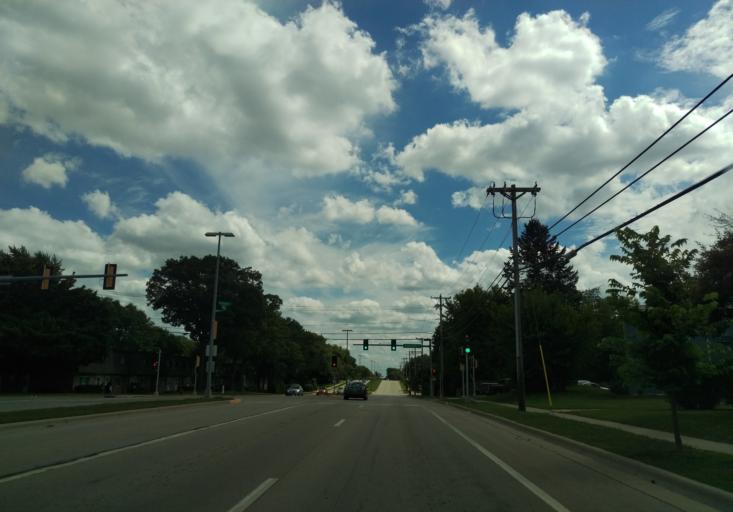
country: US
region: Wisconsin
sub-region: Dane County
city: Maple Bluff
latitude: 43.1400
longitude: -89.3887
